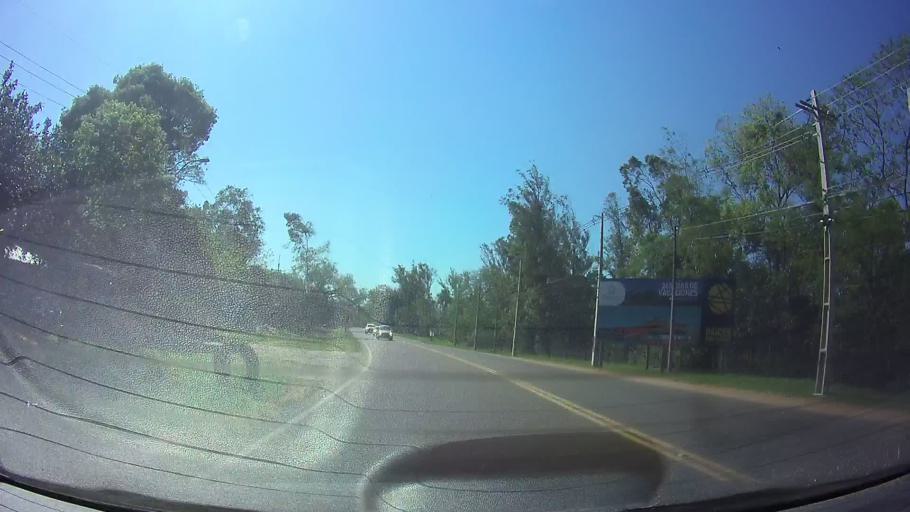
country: PY
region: Cordillera
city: San Bernardino
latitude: -25.3345
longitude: -57.2732
